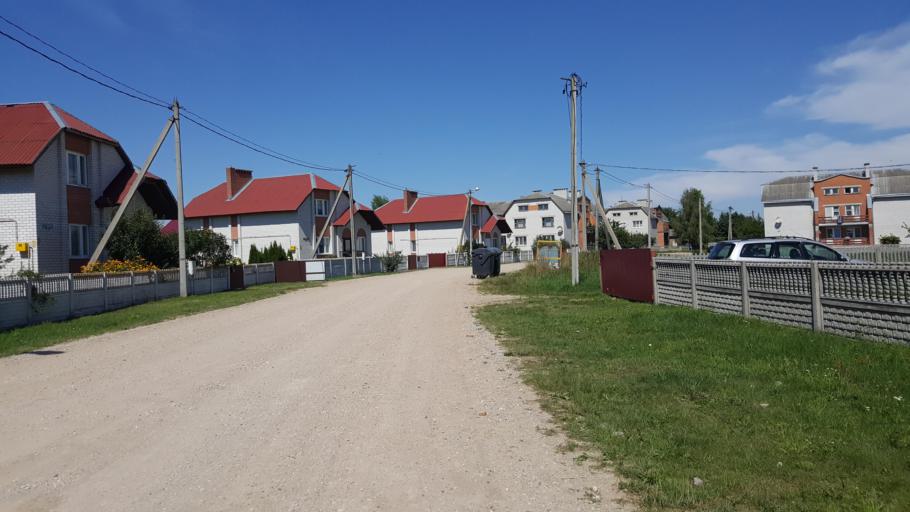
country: BY
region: Brest
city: Charnawchytsy
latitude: 52.2620
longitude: 23.5838
